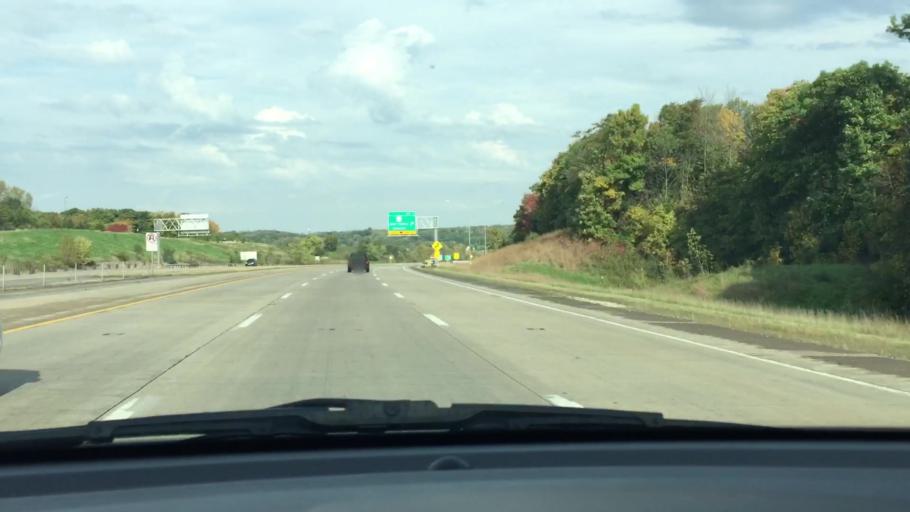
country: US
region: Iowa
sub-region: Scott County
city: Le Claire
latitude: 41.5686
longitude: -90.3562
